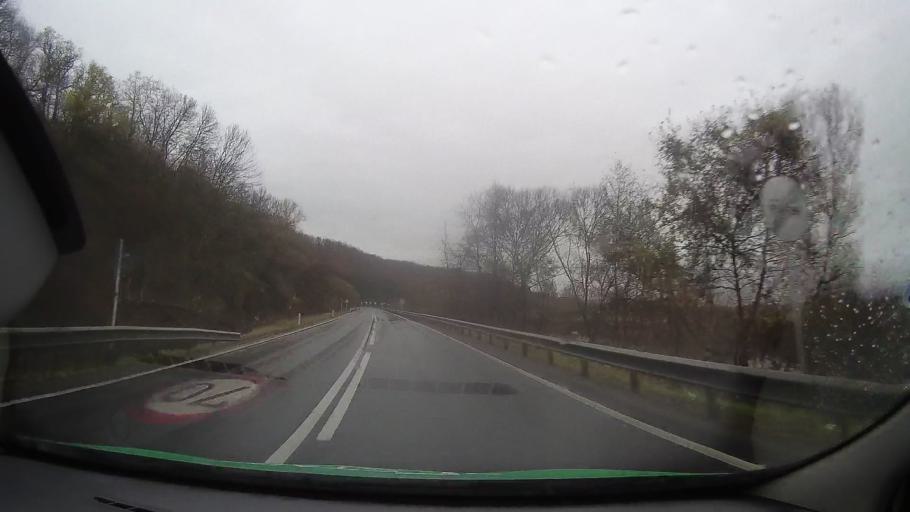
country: RO
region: Mures
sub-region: Comuna Brancovenesti
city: Brancovenesti
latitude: 46.8636
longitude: 24.7685
